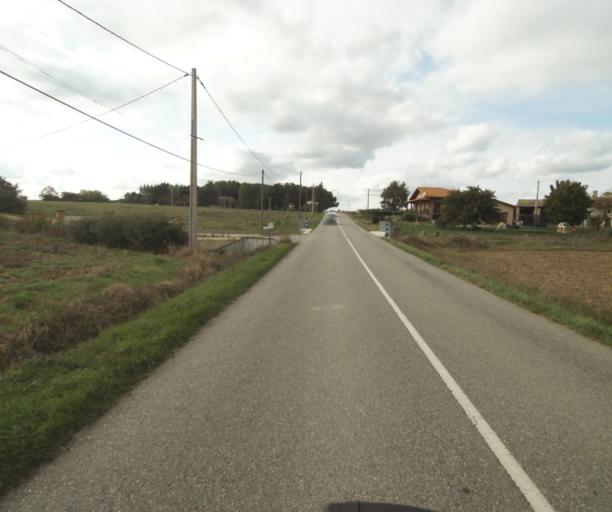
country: FR
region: Midi-Pyrenees
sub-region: Departement du Tarn-et-Garonne
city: Verdun-sur-Garonne
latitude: 43.8515
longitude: 1.1385
